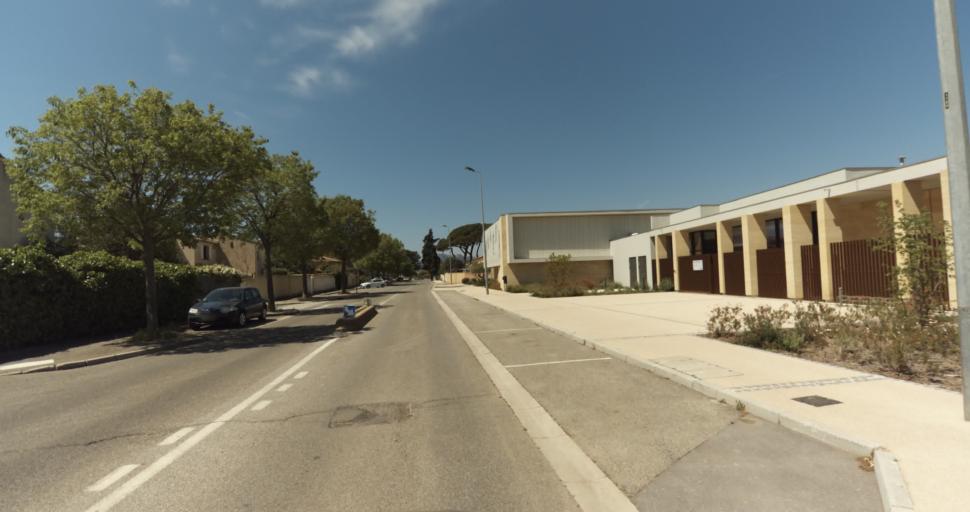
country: FR
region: Provence-Alpes-Cote d'Azur
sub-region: Departement du Var
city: La Crau
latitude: 43.1463
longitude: 6.0823
